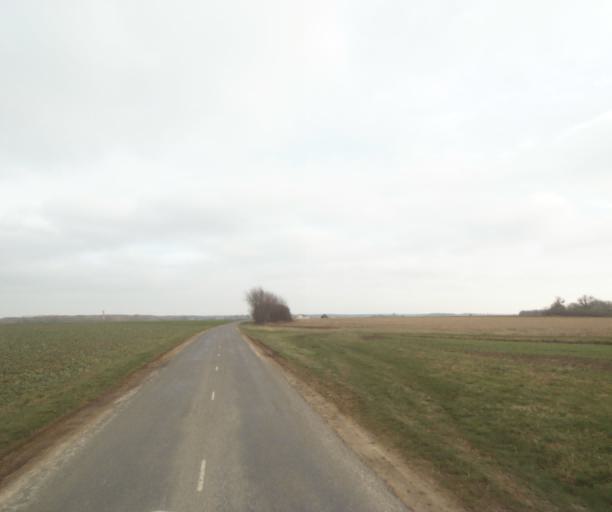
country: FR
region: Champagne-Ardenne
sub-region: Departement de la Haute-Marne
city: Villiers-en-Lieu
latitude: 48.6739
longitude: 4.8526
